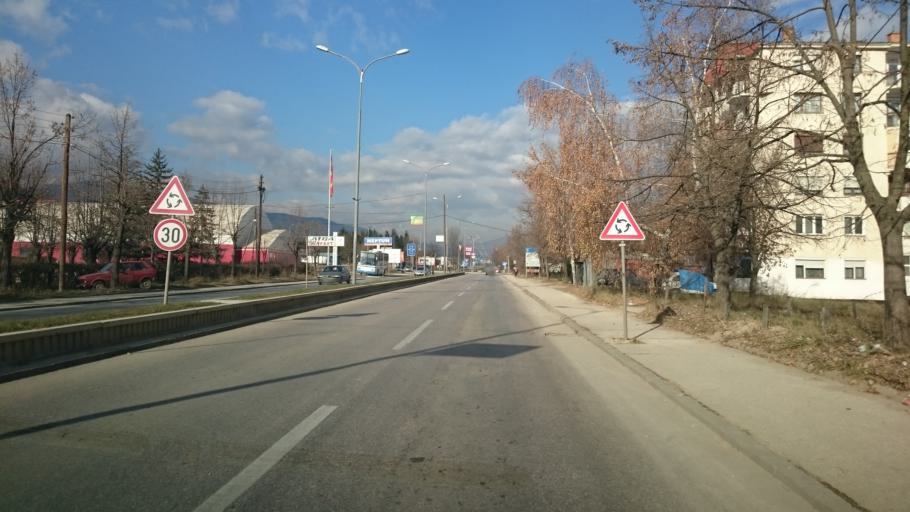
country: MK
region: Kicevo
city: Kicevo
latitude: 41.5111
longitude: 20.9524
